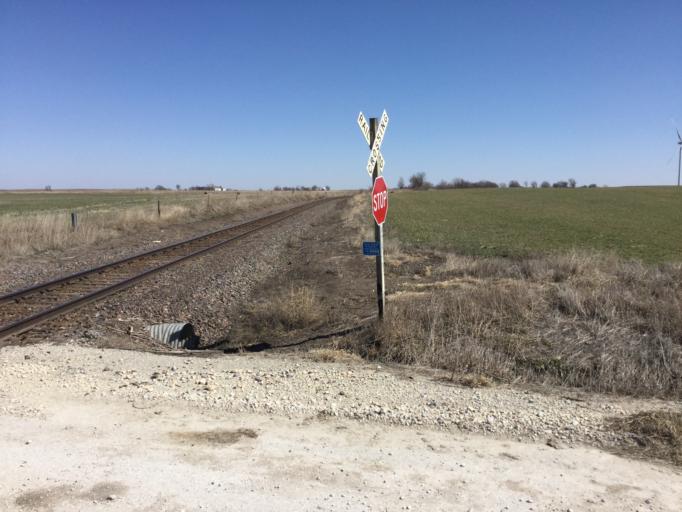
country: US
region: Kansas
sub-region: Marshall County
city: Marysville
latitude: 39.8939
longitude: -96.3702
